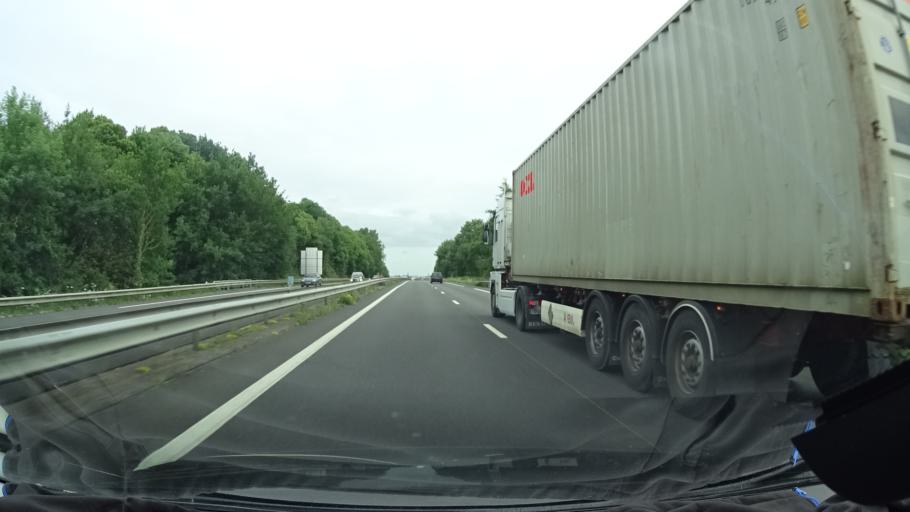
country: FR
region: Brittany
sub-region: Departement des Cotes-d'Armor
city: Saint-Samson-sur-Rance
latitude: 48.4894
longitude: -2.0415
